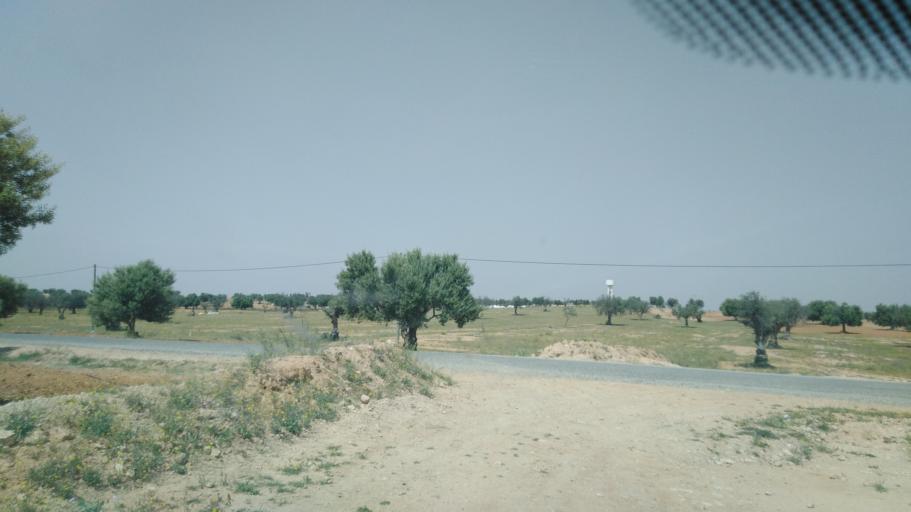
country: TN
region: Safaqis
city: Sfax
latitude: 34.7490
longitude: 10.5666
